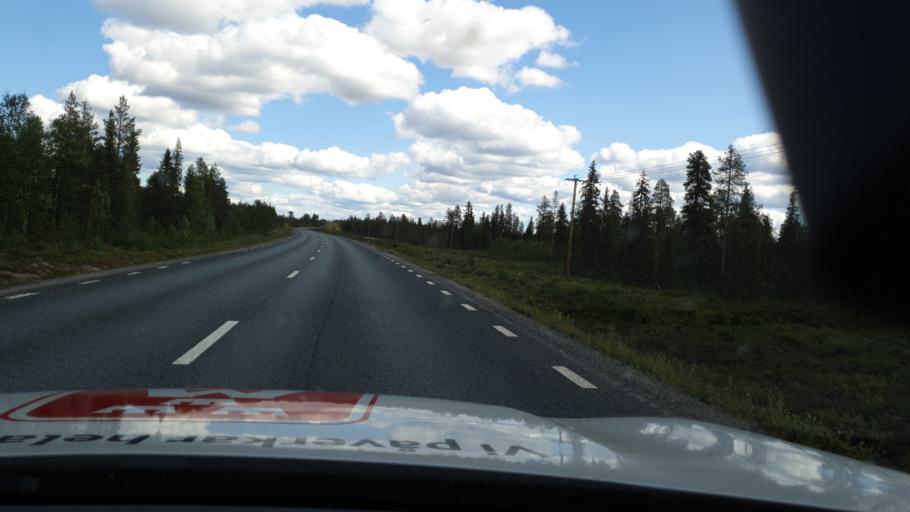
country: SE
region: Vaesterbotten
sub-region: Sorsele Kommun
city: Sorsele
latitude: 65.5596
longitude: 17.8018
